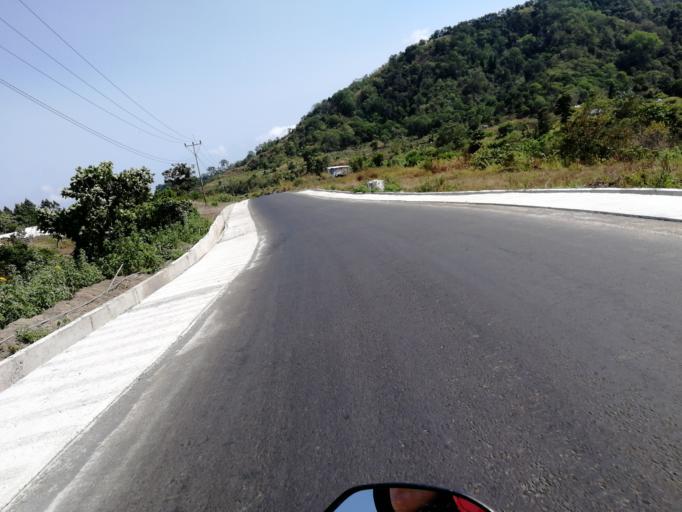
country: ID
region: West Nusa Tenggara
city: Lelongken
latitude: -8.3488
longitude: 116.5089
